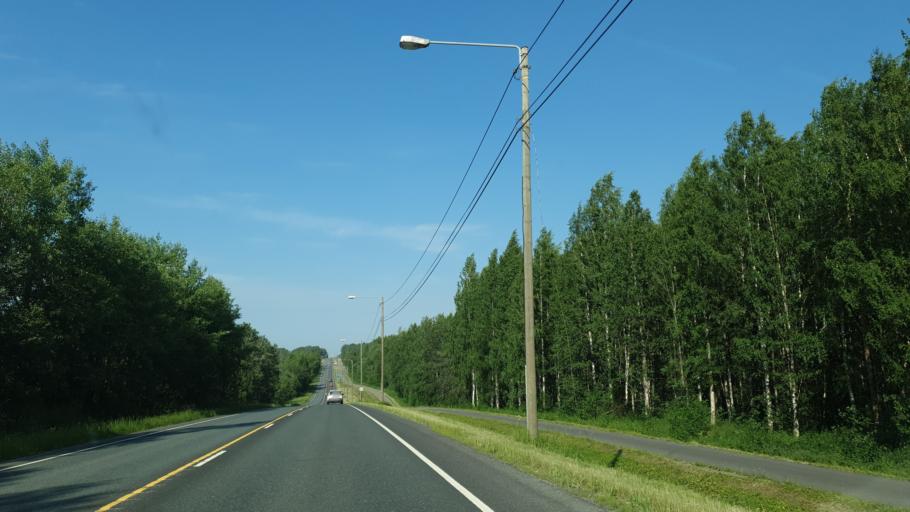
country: FI
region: Northern Savo
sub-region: Kuopio
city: Siilinjaervi
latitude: 63.0927
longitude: 27.7233
